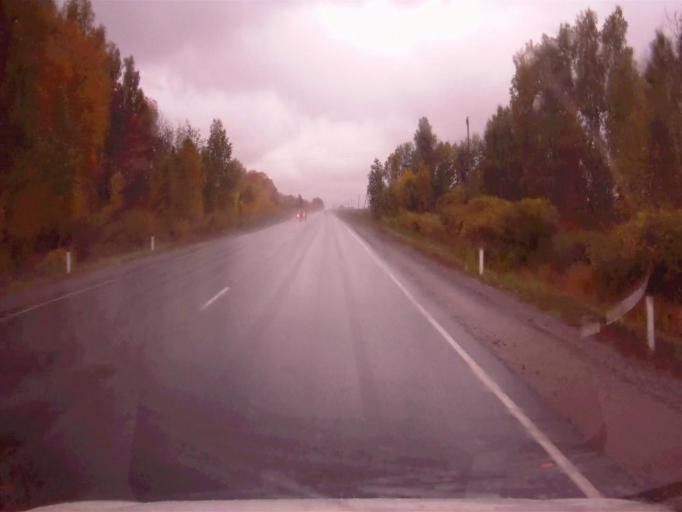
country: RU
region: Chelyabinsk
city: Argayash
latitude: 55.4241
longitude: 61.0074
